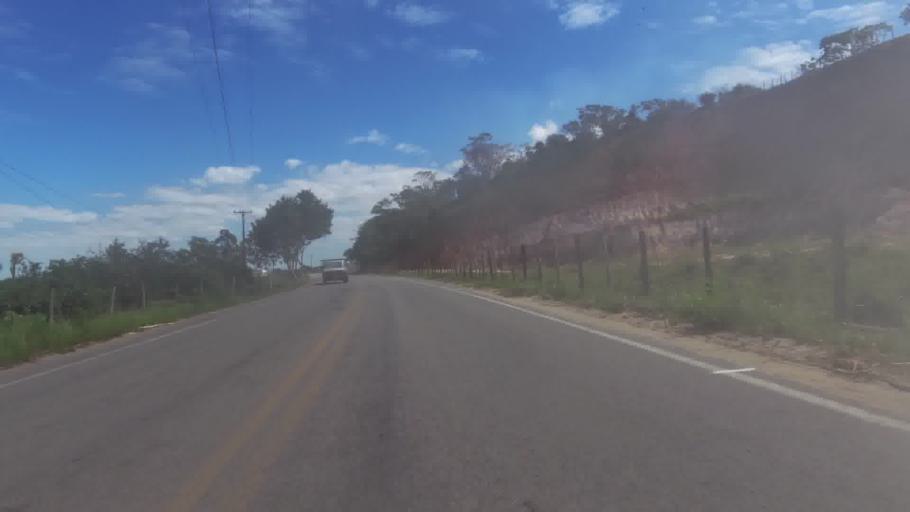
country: BR
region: Espirito Santo
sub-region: Marataizes
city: Marataizes
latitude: -21.1991
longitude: -40.9516
